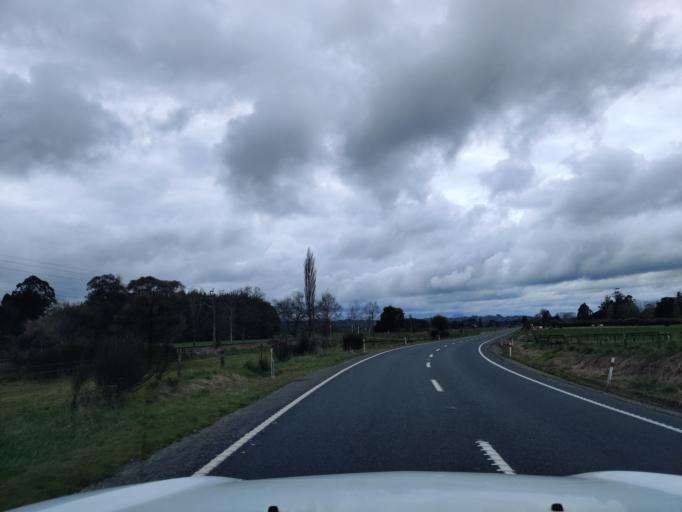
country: NZ
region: Waikato
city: Turangi
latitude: -39.0230
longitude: 175.3800
